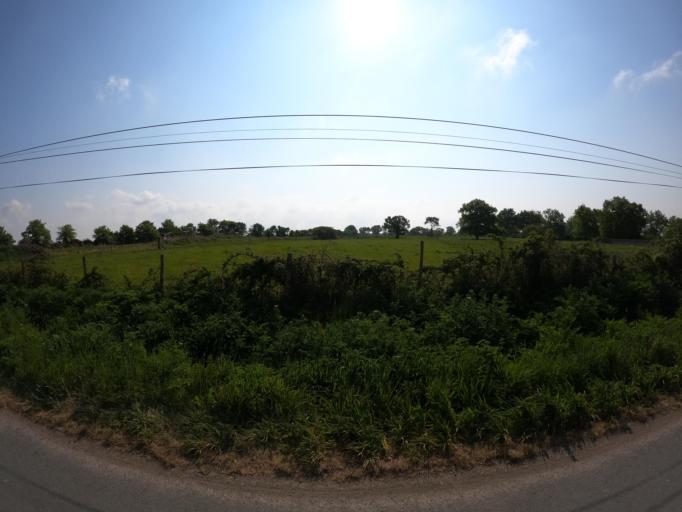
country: FR
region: Pays de la Loire
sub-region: Departement de la Vendee
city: Treize-Septiers
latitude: 47.0016
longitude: -1.2565
